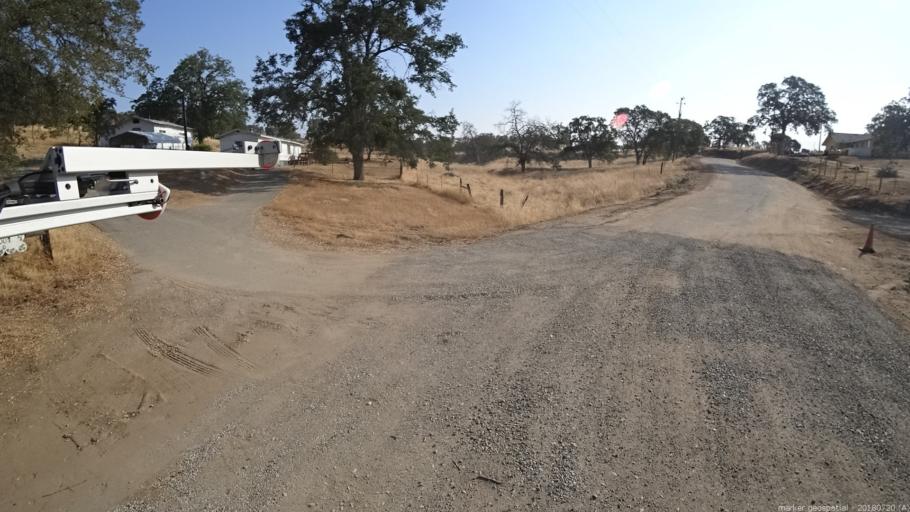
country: US
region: California
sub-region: Madera County
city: Yosemite Lakes
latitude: 37.2193
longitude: -119.9085
